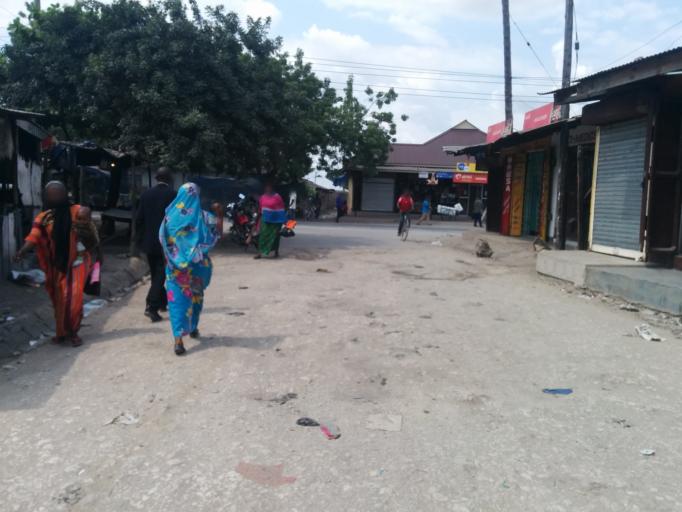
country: TZ
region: Dar es Salaam
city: Dar es Salaam
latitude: -6.8636
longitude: 39.2511
